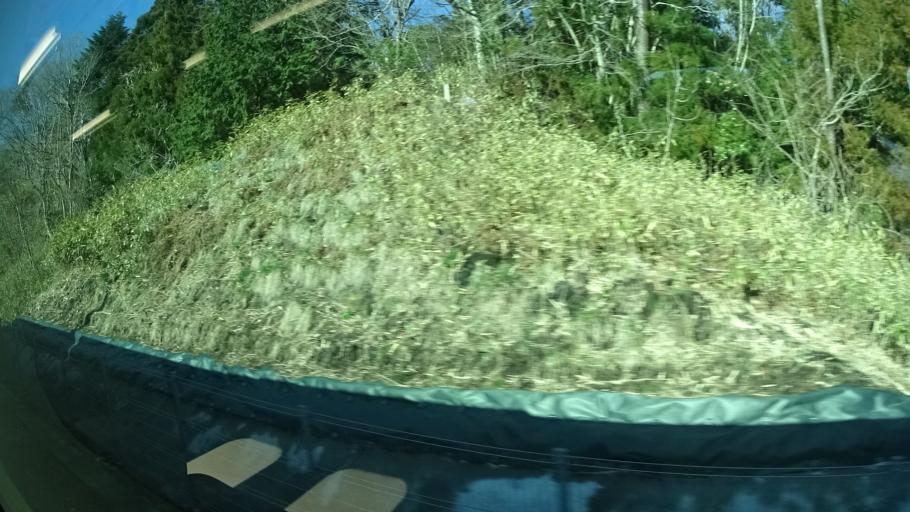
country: JP
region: Fukushima
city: Namie
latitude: 37.3765
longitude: 140.9911
